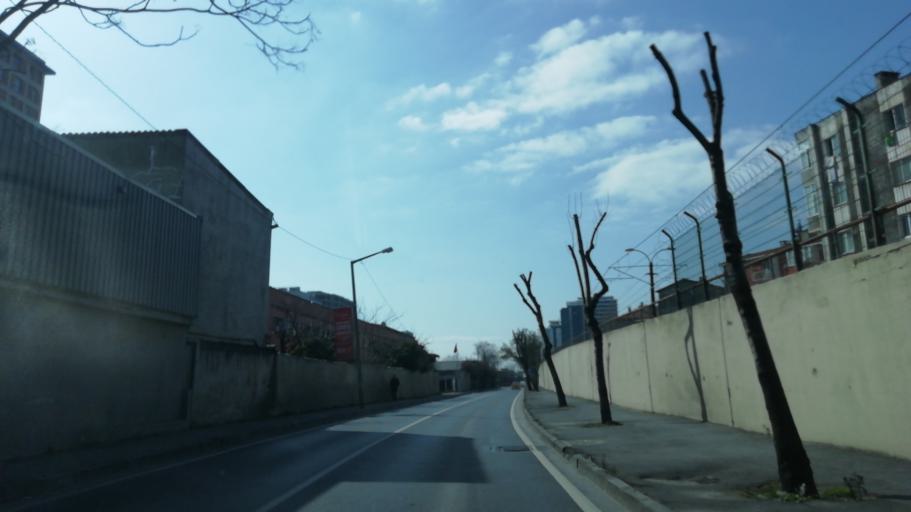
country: TR
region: Istanbul
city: guengoeren merter
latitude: 41.0124
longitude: 28.8997
